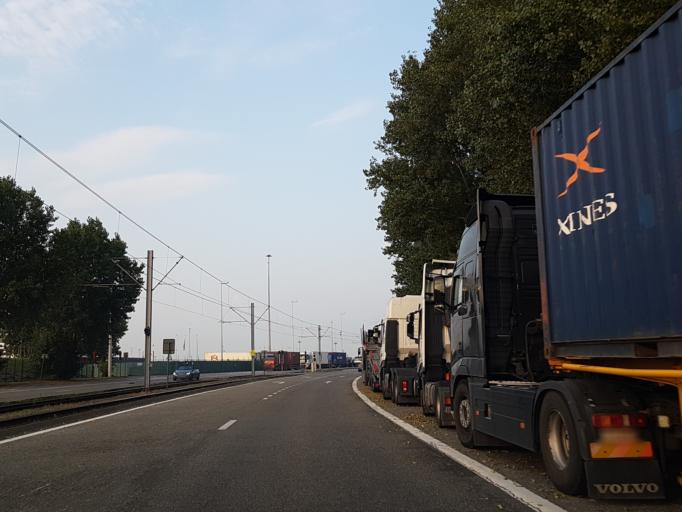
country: BE
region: Flanders
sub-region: Provincie West-Vlaanderen
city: Zeebrugge
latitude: 51.3349
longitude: 3.2101
